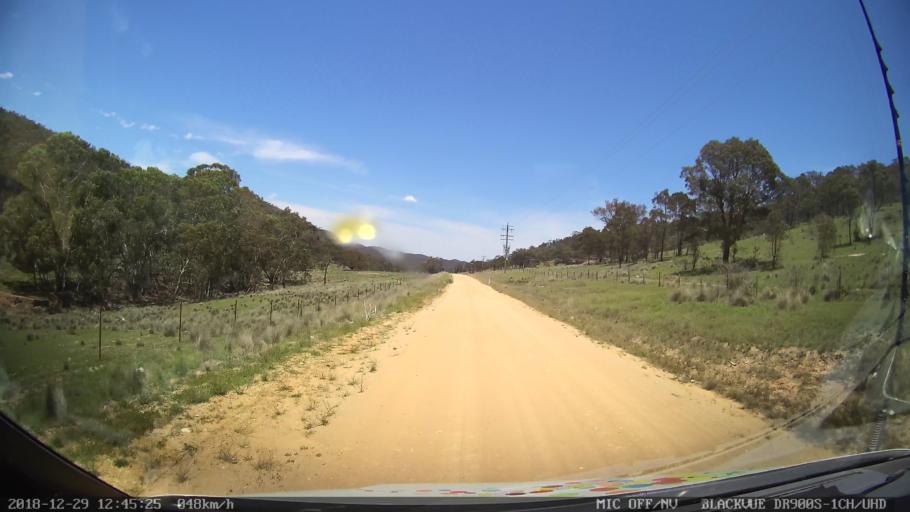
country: AU
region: Australian Capital Territory
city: Macarthur
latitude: -35.6348
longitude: 149.2147
